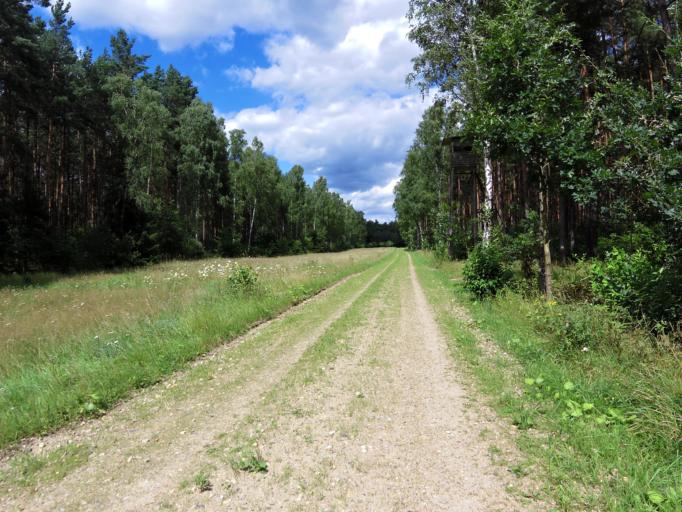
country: DE
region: Brandenburg
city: Lychen
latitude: 53.1651
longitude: 13.3825
